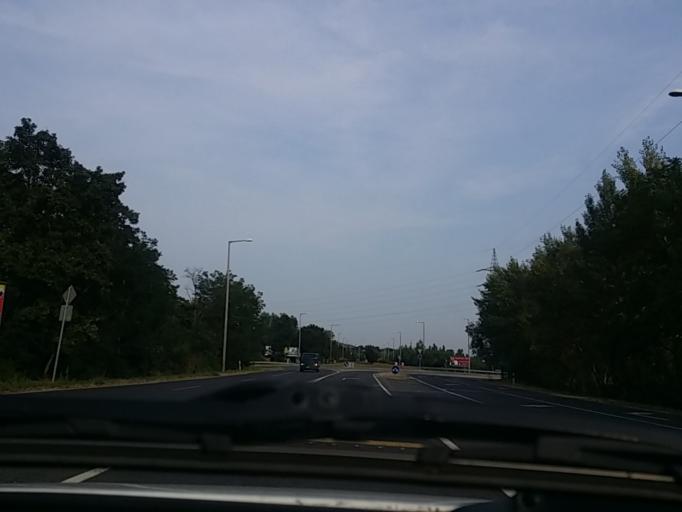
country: HU
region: Pest
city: Toeroekbalint
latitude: 47.4621
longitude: 18.8931
